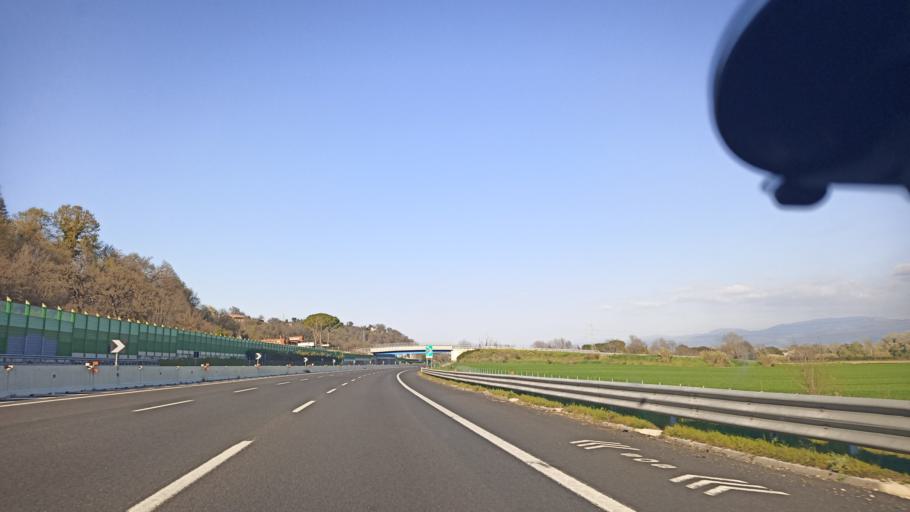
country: IT
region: Latium
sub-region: Citta metropolitana di Roma Capitale
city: Costaroni
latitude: 42.0746
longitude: 12.5408
